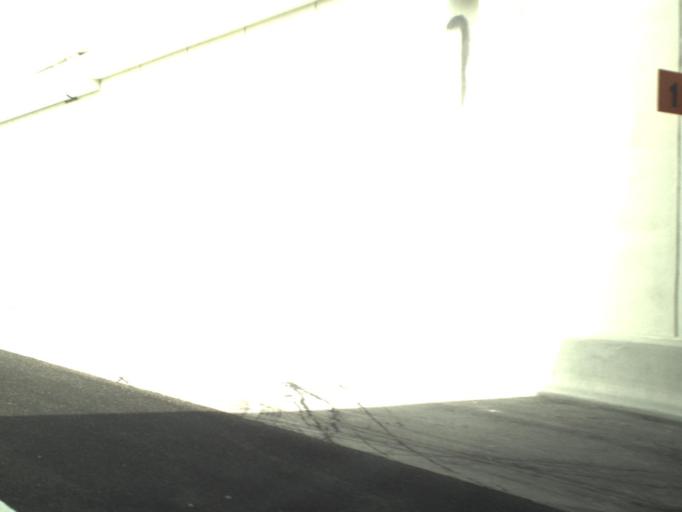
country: US
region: Florida
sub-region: Broward County
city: Dania Beach
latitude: 26.0651
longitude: -80.1410
